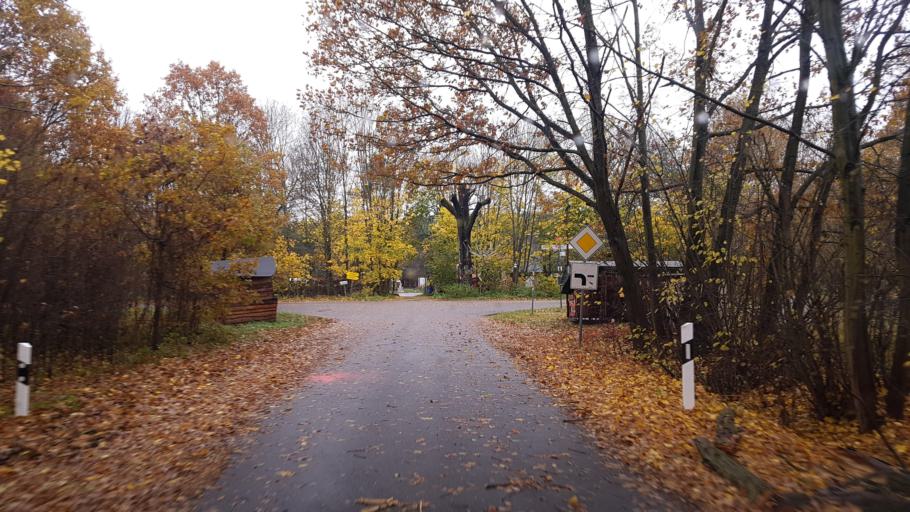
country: DE
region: Brandenburg
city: Altdobern
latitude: 51.6700
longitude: 14.1093
